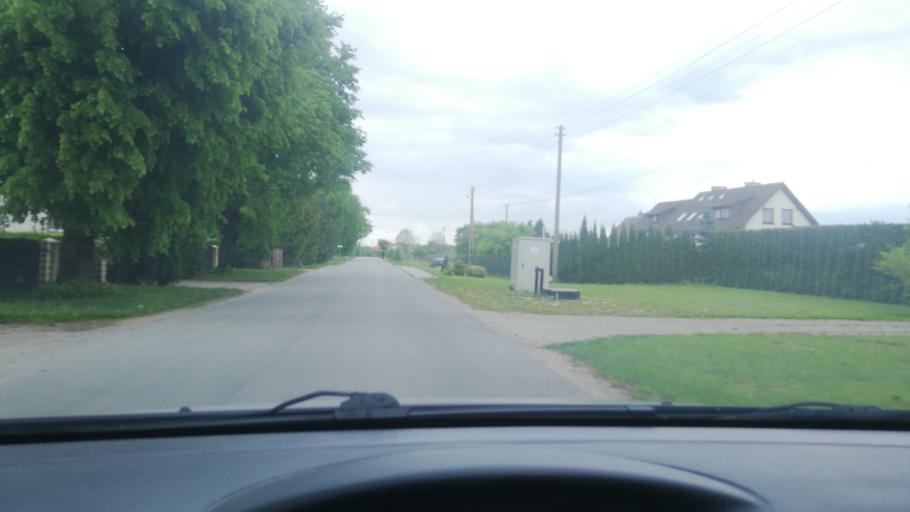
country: LT
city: Priekule
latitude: 55.6436
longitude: 21.2950
